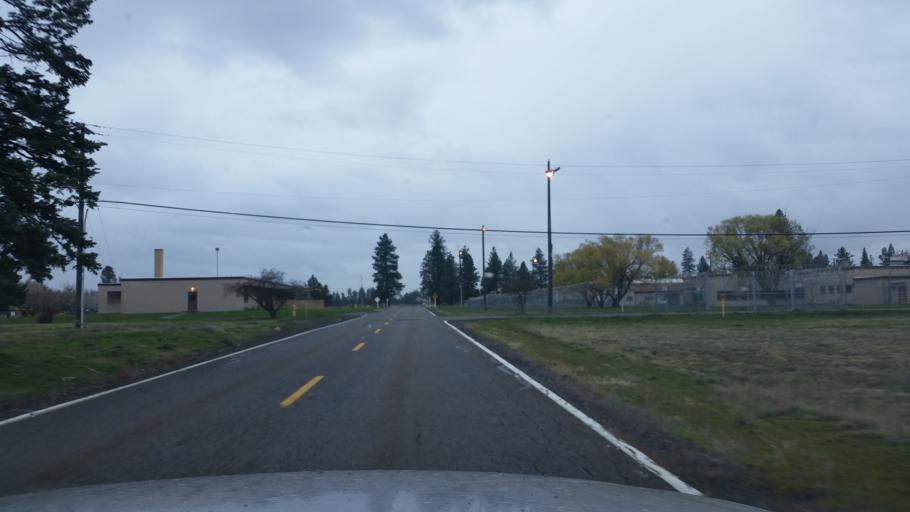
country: US
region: Washington
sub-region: Spokane County
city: Airway Heights
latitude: 47.6231
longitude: -117.5133
